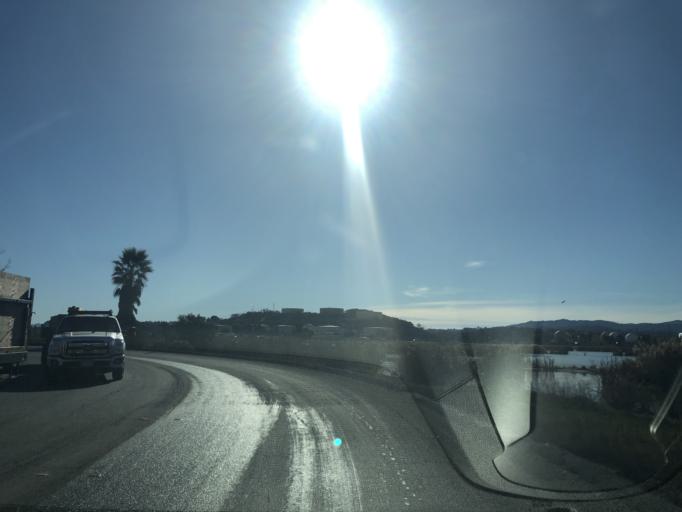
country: US
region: California
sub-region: Contra Costa County
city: Vine Hill
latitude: 38.0257
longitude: -122.1016
